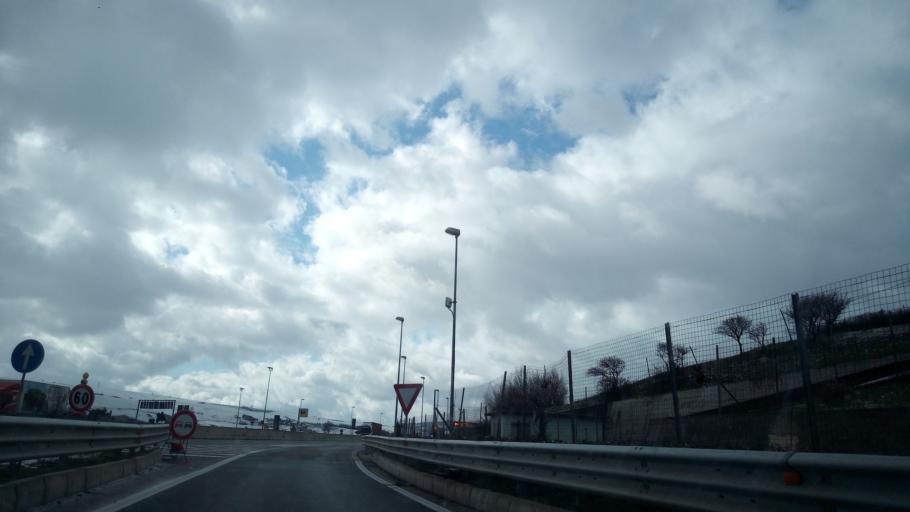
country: IT
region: Campania
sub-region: Provincia di Avellino
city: Scampitella
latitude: 41.0658
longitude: 15.3148
